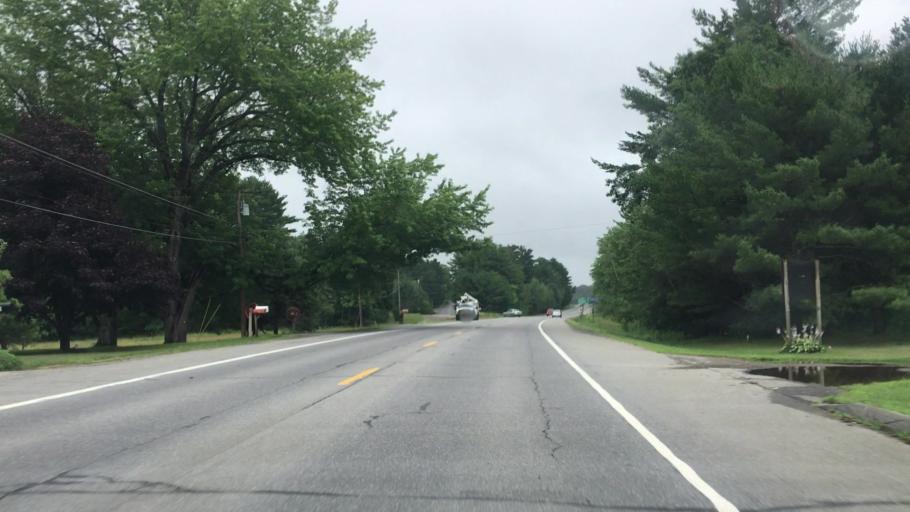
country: US
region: Maine
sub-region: Kennebec County
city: Windsor
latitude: 44.2647
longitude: -69.5615
